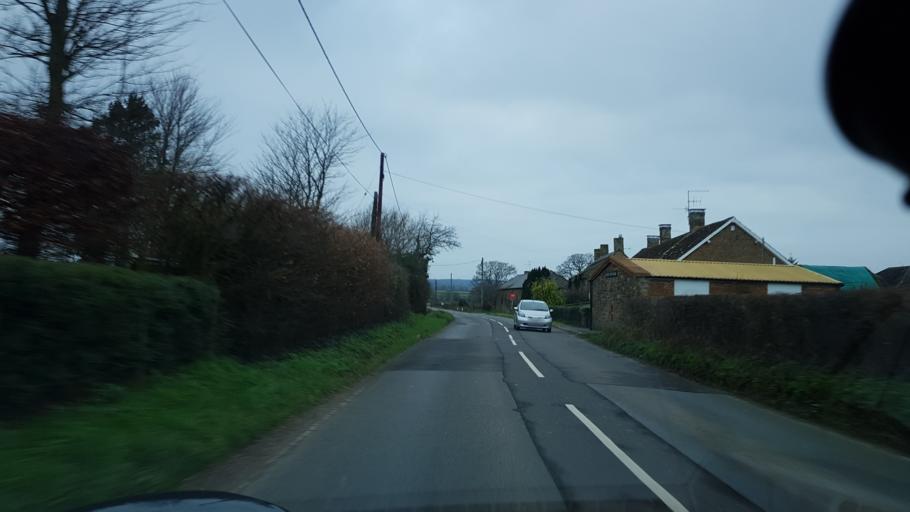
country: GB
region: England
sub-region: Somerset
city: Ilminster
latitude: 50.9127
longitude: -2.9261
